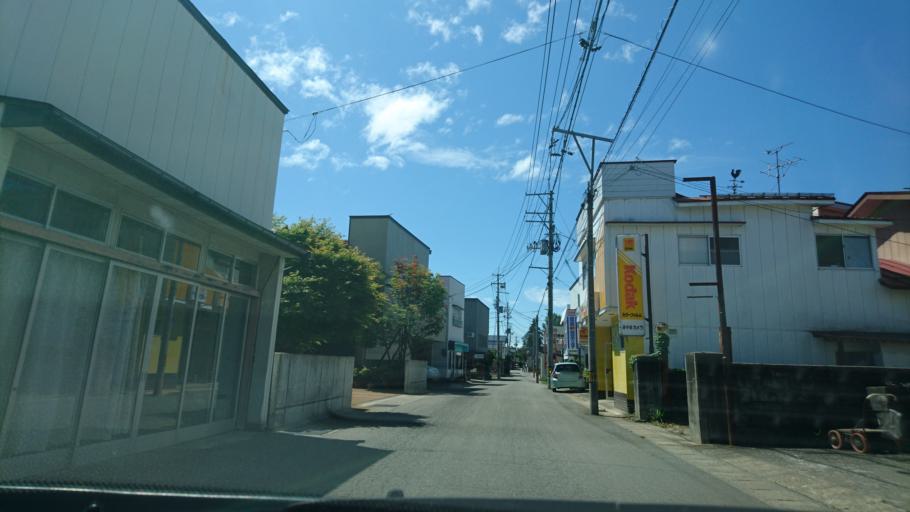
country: JP
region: Akita
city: Kakunodatemachi
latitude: 39.5899
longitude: 140.5642
